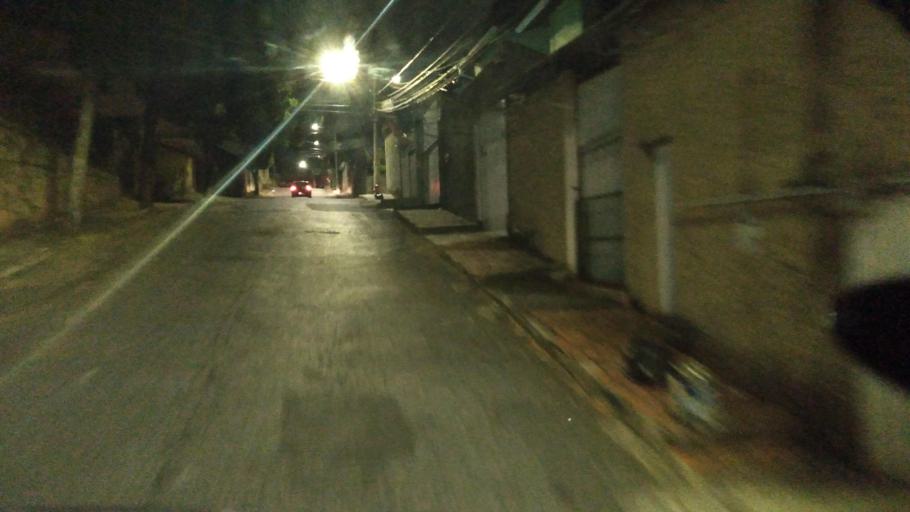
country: BR
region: Minas Gerais
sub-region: Belo Horizonte
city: Belo Horizonte
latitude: -19.8884
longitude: -43.9587
